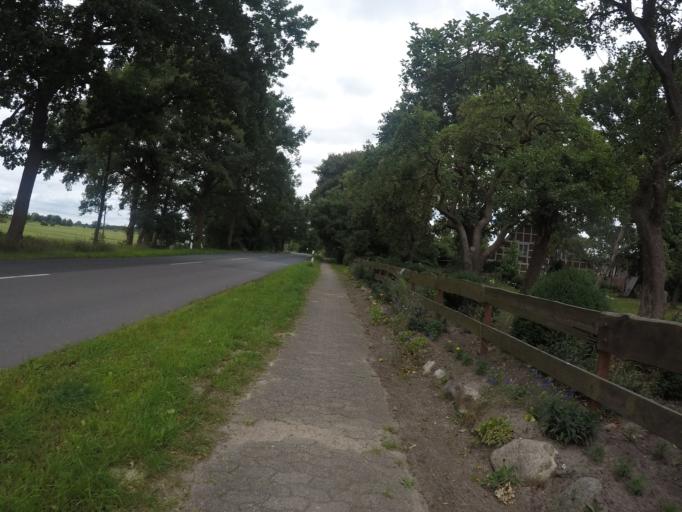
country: DE
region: Lower Saxony
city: Himmelpforten
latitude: 53.6300
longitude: 9.3048
